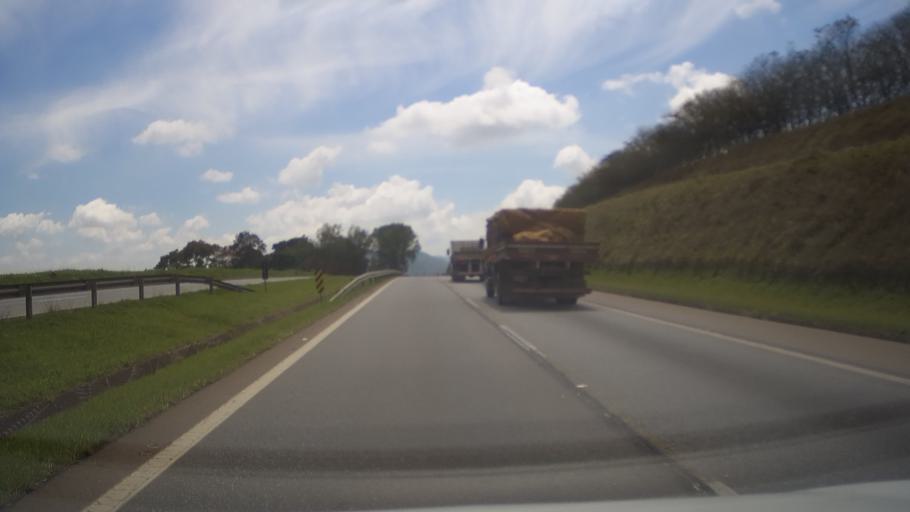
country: BR
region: Minas Gerais
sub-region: Santa Rita Do Sapucai
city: Santa Rita do Sapucai
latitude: -22.1006
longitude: -45.7209
